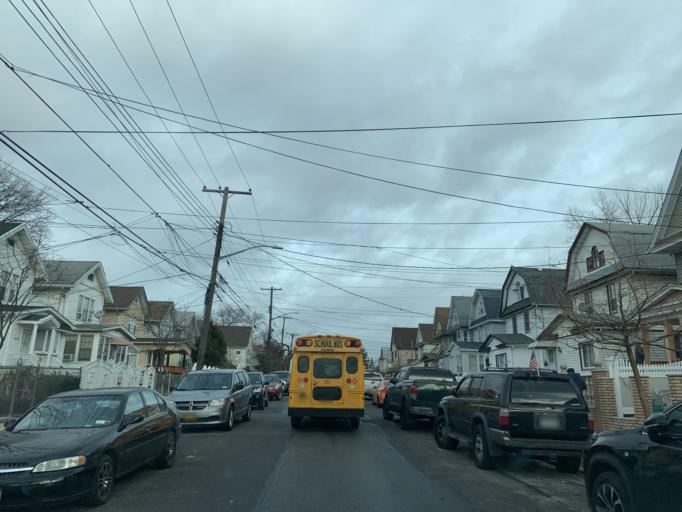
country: US
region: New York
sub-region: Queens County
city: Jamaica
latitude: 40.6892
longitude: -73.8115
